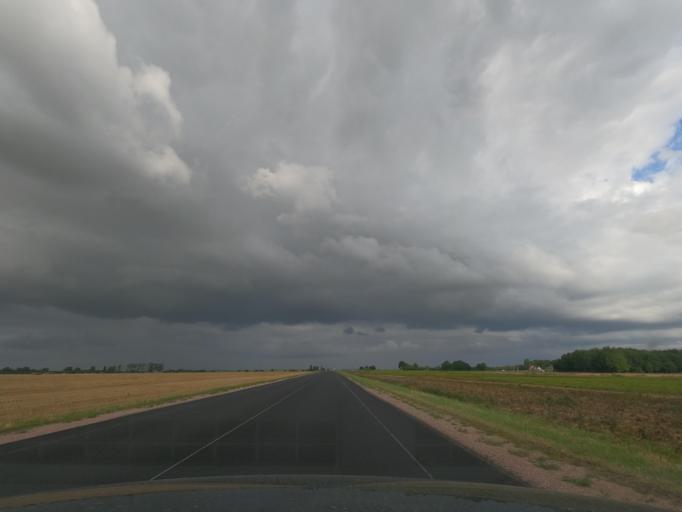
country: FR
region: Haute-Normandie
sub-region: Departement de l'Eure
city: Menneval
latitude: 49.1132
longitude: 0.6105
